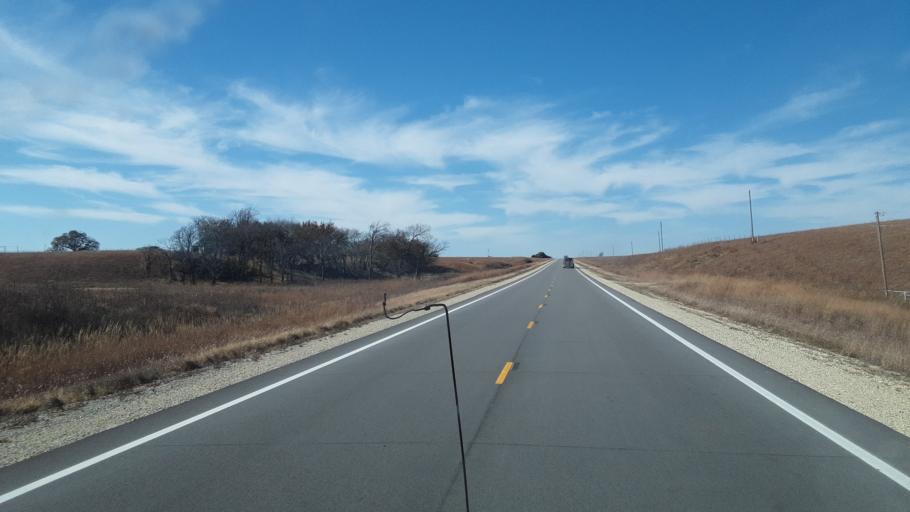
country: US
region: Kansas
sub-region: Marion County
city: Marion
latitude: 38.3628
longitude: -96.7850
